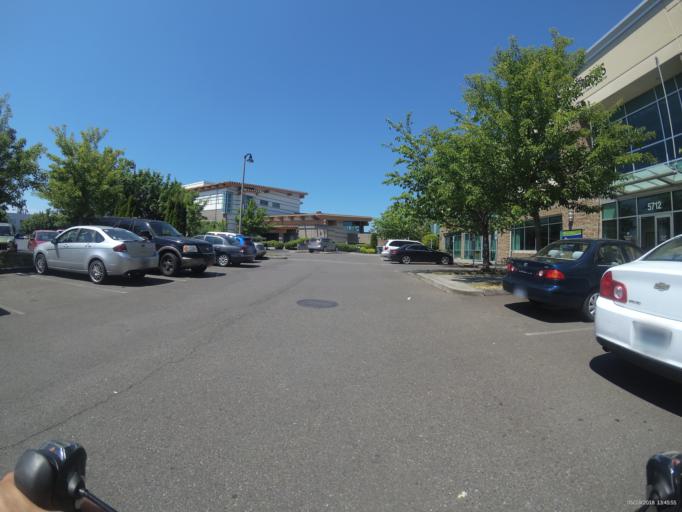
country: US
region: Washington
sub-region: Pierce County
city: Lakewood
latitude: 47.1607
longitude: -122.5154
